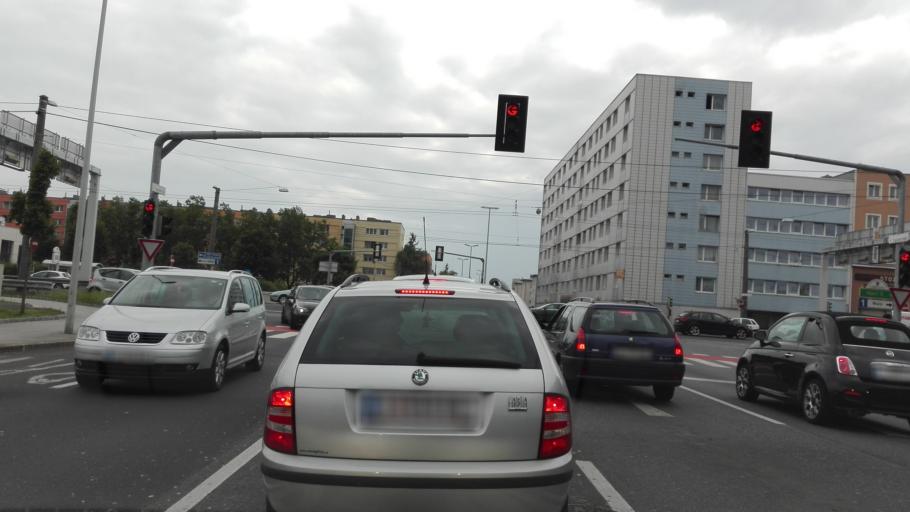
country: AT
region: Upper Austria
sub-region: Politischer Bezirk Linz-Land
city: Leonding
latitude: 48.2542
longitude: 14.2824
